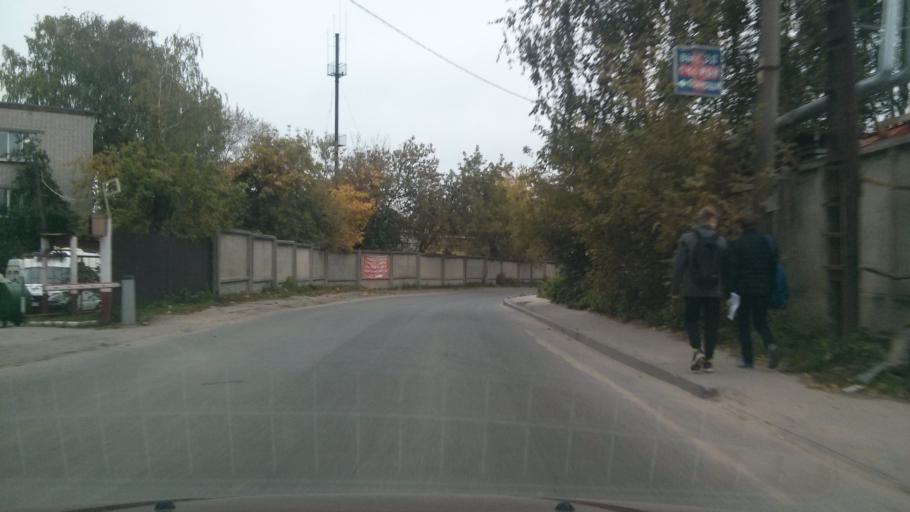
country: RU
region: Nizjnij Novgorod
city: Nizhniy Novgorod
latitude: 56.3093
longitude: 44.0075
